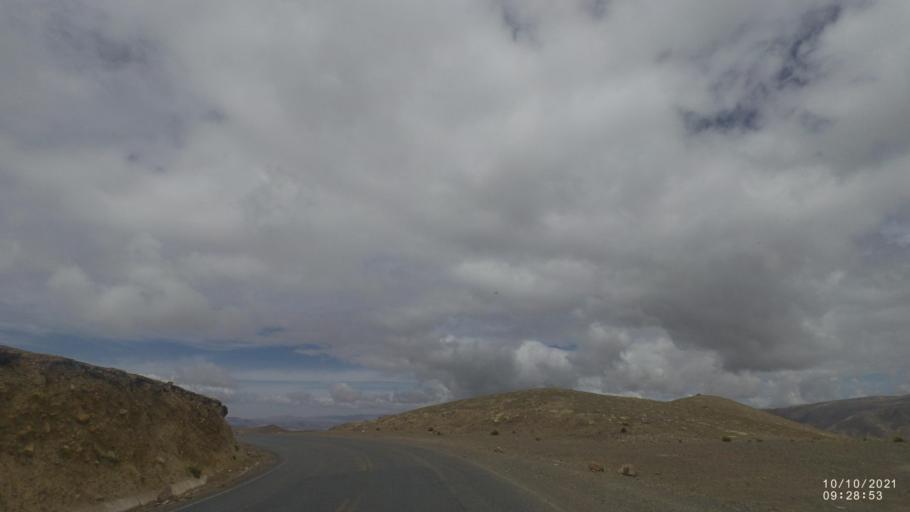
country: BO
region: La Paz
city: Quime
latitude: -17.1094
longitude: -67.3259
